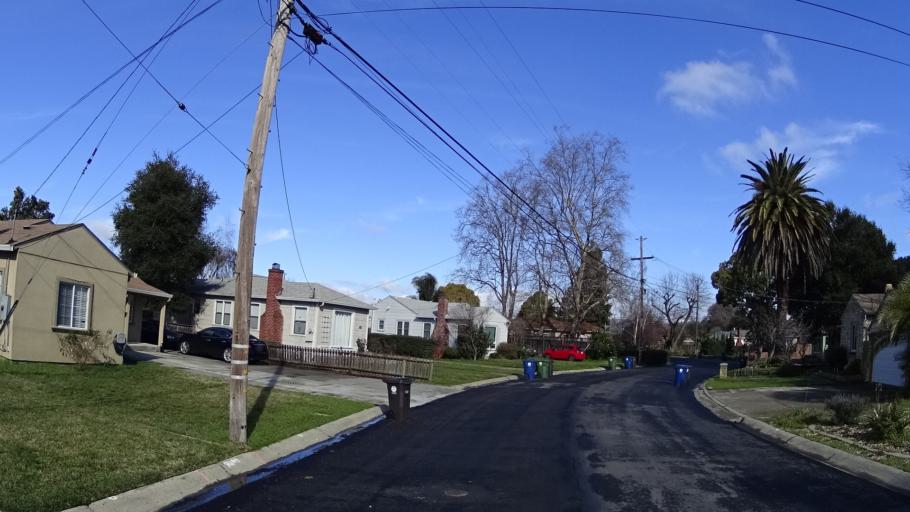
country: US
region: California
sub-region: Alameda County
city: Castro Valley
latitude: 37.6891
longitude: -122.0808
